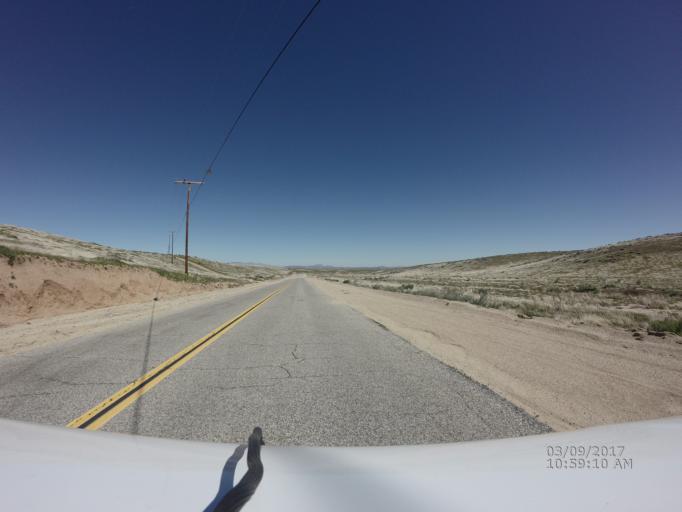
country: US
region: California
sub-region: Los Angeles County
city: Green Valley
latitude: 34.6988
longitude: -118.3774
